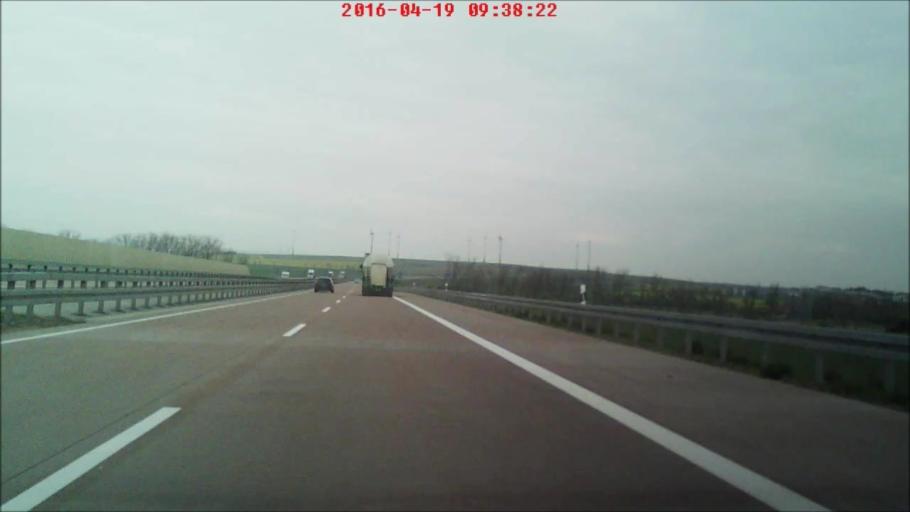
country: DE
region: Thuringia
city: Artern
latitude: 51.3626
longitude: 11.2752
